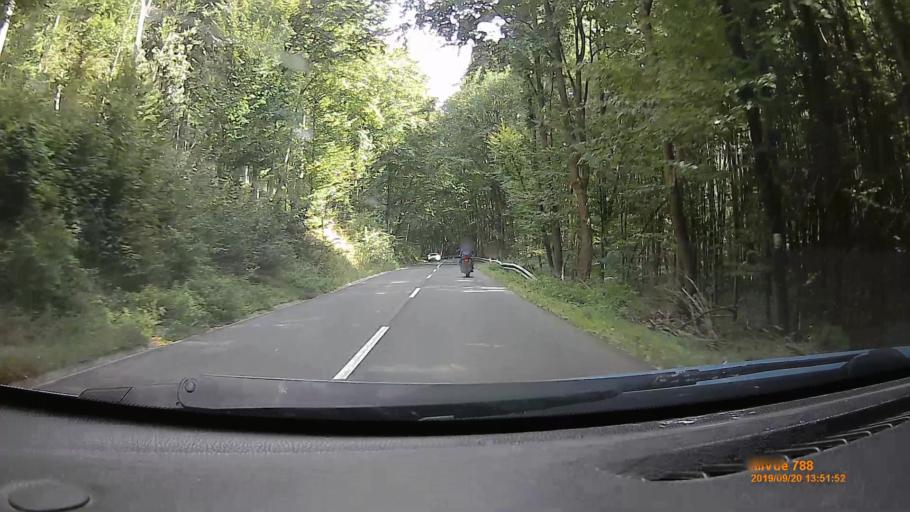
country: HU
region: Borsod-Abauj-Zemplen
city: Saly
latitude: 48.0709
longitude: 20.5992
